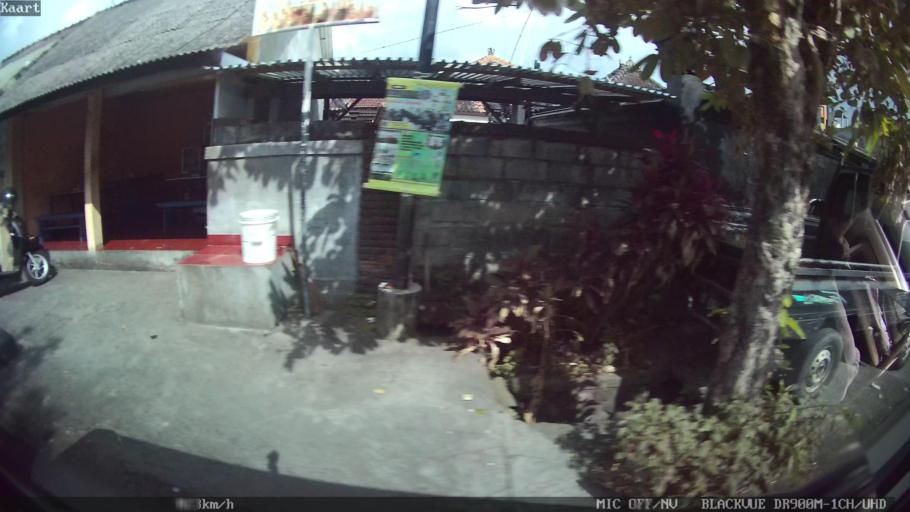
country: ID
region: Bali
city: Banjar Karangsuling
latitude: -8.6120
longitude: 115.2002
